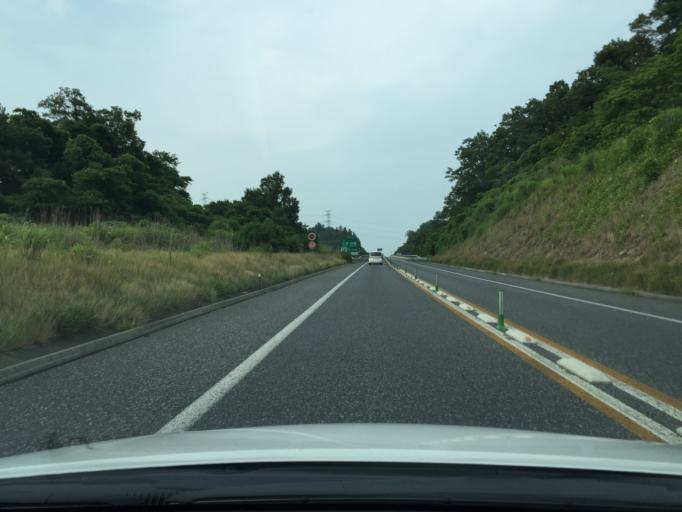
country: JP
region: Fukushima
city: Iwaki
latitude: 37.2289
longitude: 140.9785
